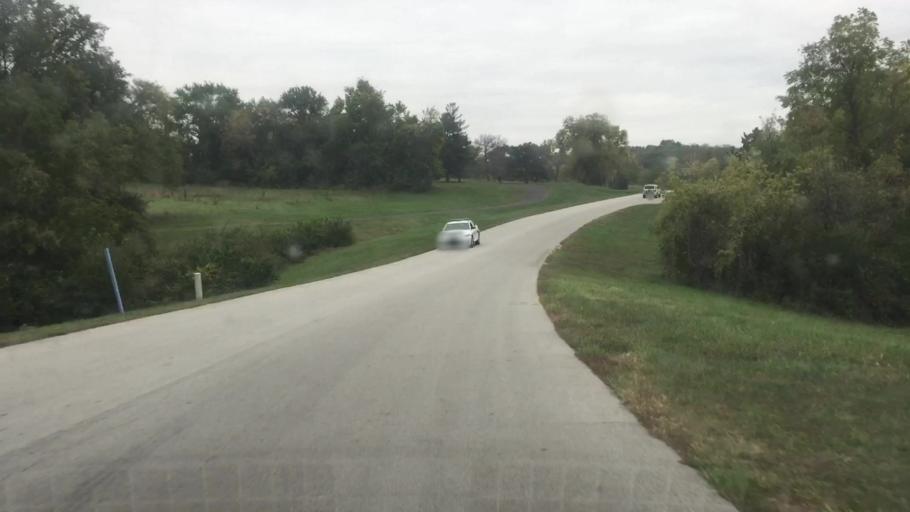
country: US
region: Kansas
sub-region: Johnson County
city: Lenexa
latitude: 38.9871
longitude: -94.7940
